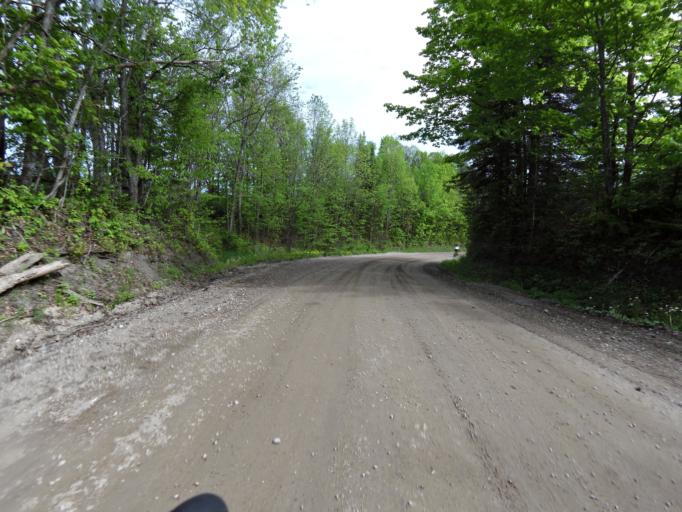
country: CA
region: Quebec
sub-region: Outaouais
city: Wakefield
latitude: 45.7181
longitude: -75.8903
